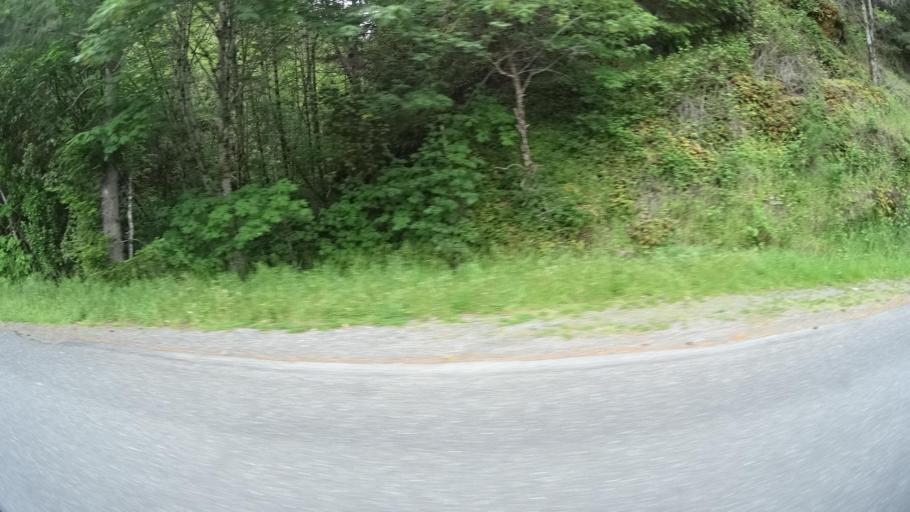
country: US
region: California
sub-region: Humboldt County
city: Willow Creek
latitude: 40.9474
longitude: -123.6108
